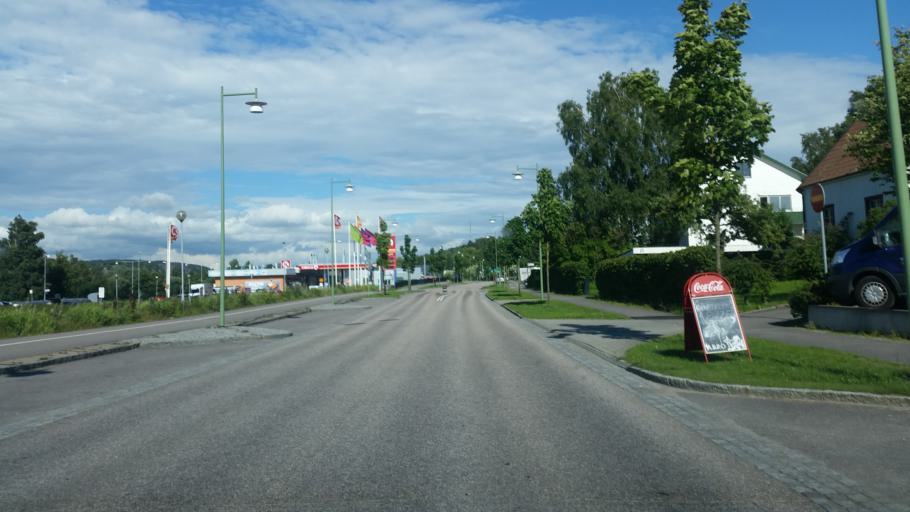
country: SE
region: Vaestra Goetaland
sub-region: Partille Kommun
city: Partille
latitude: 57.7330
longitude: 12.0776
